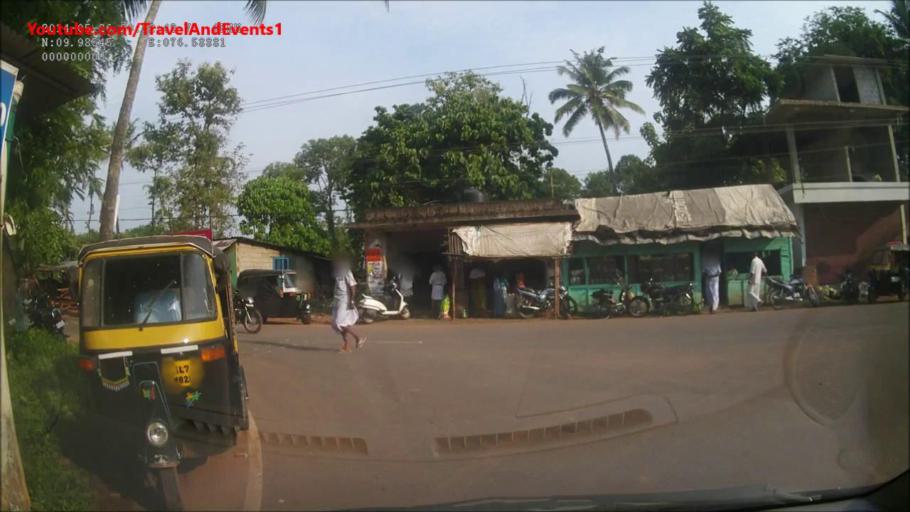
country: IN
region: Kerala
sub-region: Ernakulam
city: Muvattupula
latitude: 9.9840
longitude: 76.5890
